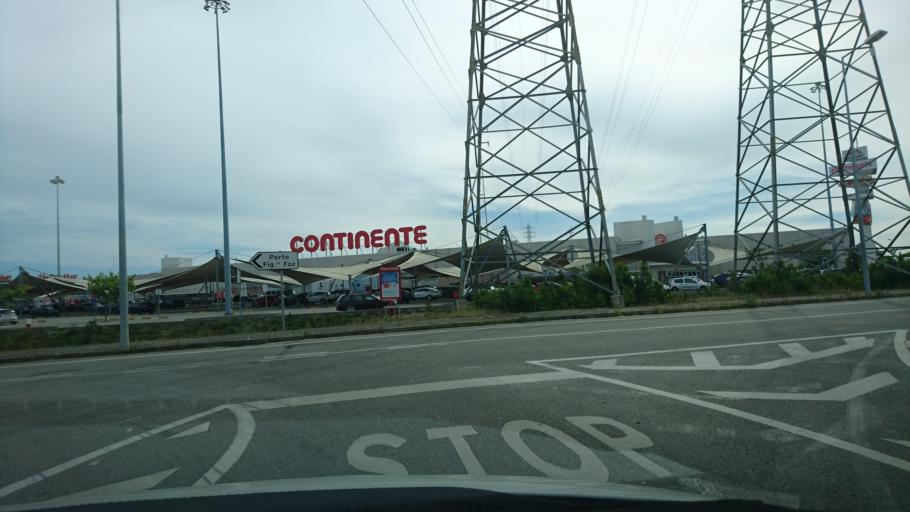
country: PT
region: Aveiro
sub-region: Aveiro
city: Aveiro
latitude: 40.6493
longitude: -8.6170
